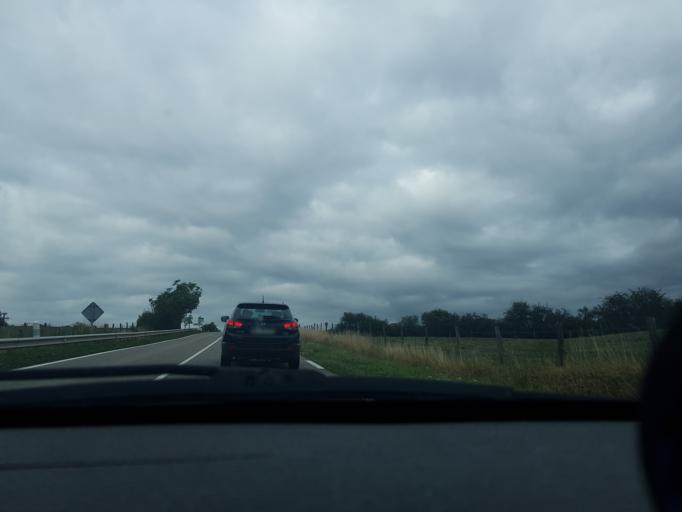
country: FR
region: Lorraine
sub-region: Departement de la Moselle
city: Chateau-Salins
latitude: 48.8850
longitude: 6.5375
